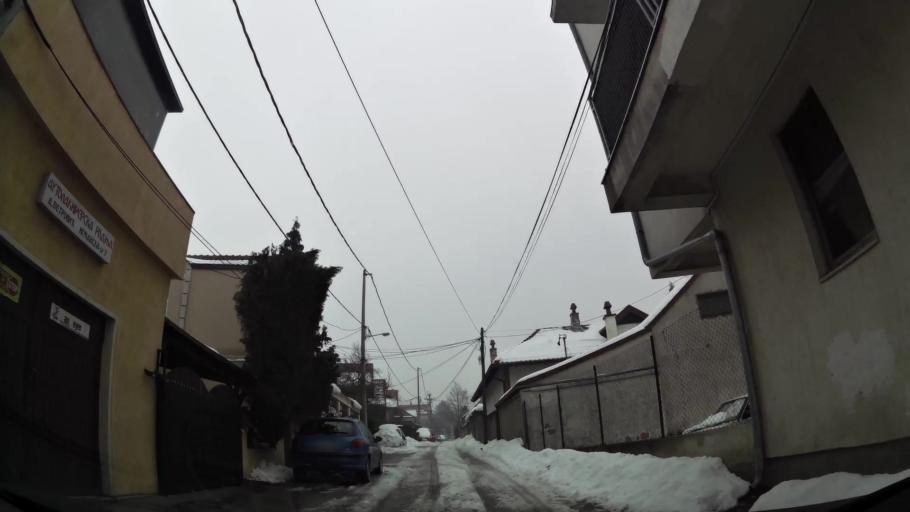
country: RS
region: Central Serbia
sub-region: Belgrade
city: Zvezdara
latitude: 44.7827
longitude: 20.5266
